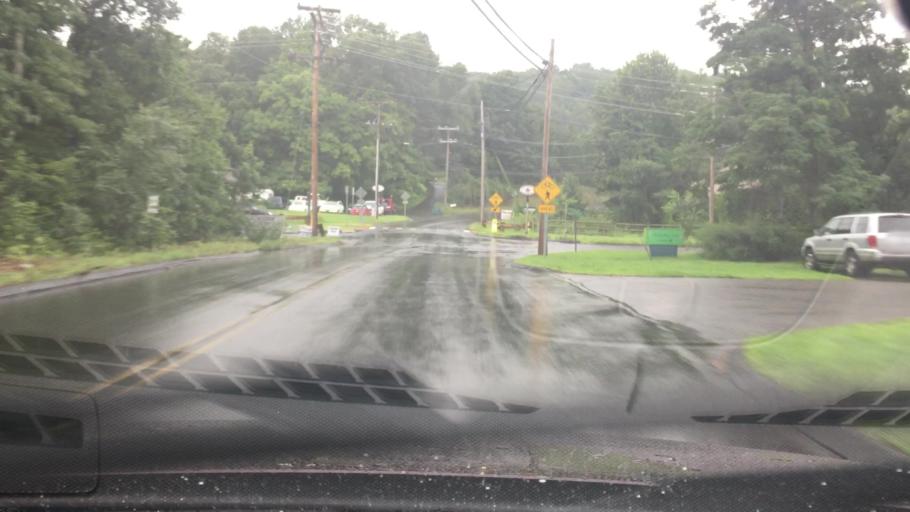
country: US
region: Connecticut
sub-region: New Haven County
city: Cheshire Village
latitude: 41.5354
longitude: -72.9021
